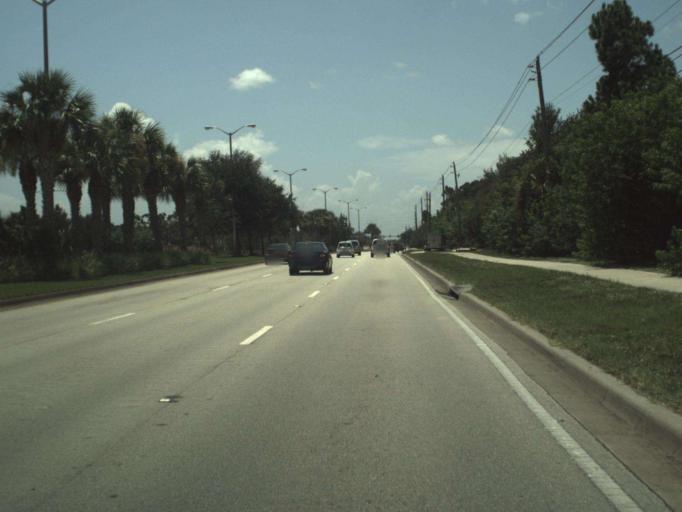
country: US
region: Florida
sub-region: Saint Lucie County
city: Port Saint Lucie
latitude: 27.2648
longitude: -80.4043
